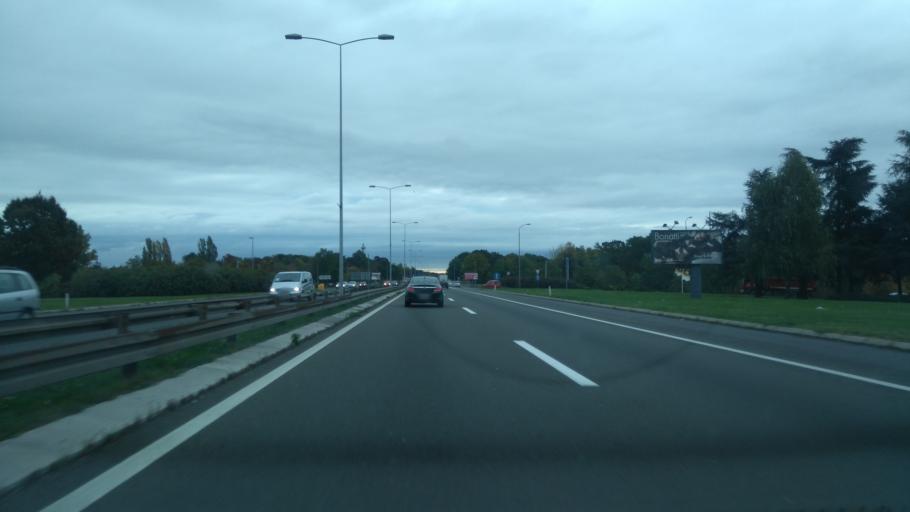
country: RS
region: Central Serbia
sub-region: Belgrade
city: Zemun
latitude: 44.8324
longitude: 20.3611
